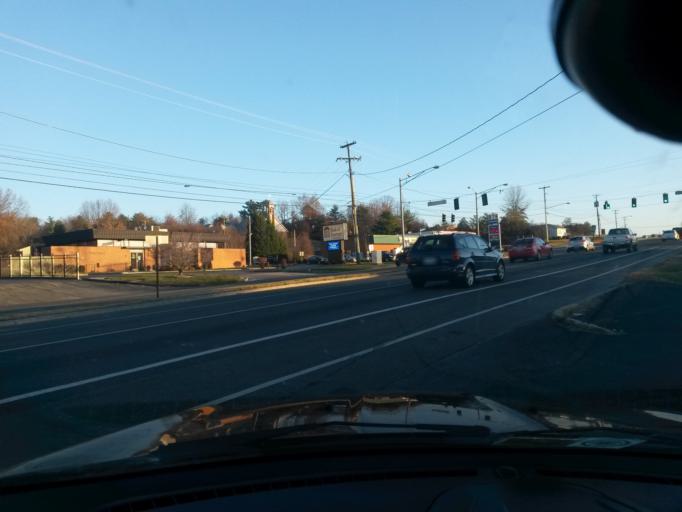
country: US
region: Virginia
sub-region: Roanoke County
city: Hollins
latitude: 37.3201
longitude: -79.9996
